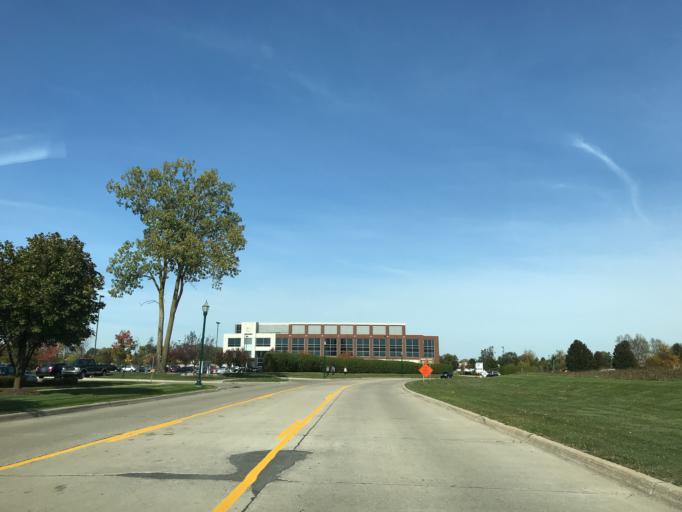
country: US
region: Michigan
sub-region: Oakland County
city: Franklin
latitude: 42.4889
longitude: -83.3037
